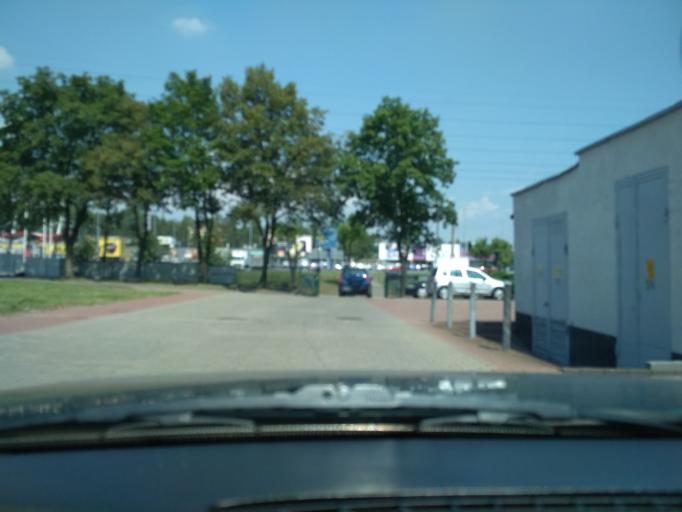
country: PL
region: Silesian Voivodeship
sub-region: Siemianowice Slaskie
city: Siemianowice Slaskie
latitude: 50.3014
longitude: 19.0133
